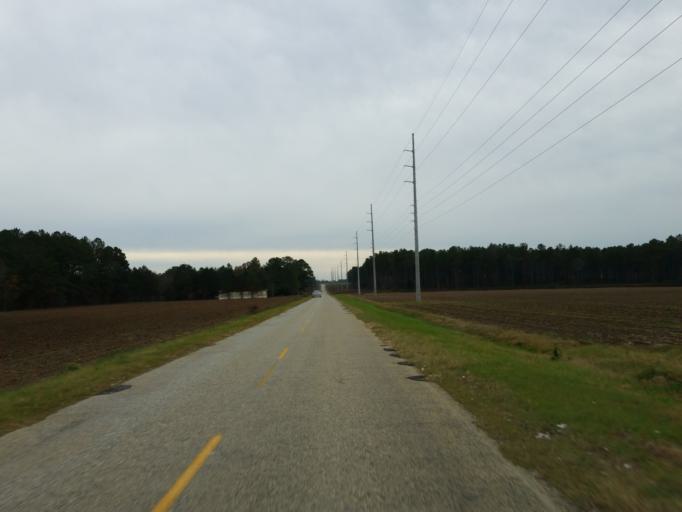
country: US
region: Georgia
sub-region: Dooly County
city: Vienna
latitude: 32.1395
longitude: -83.7612
